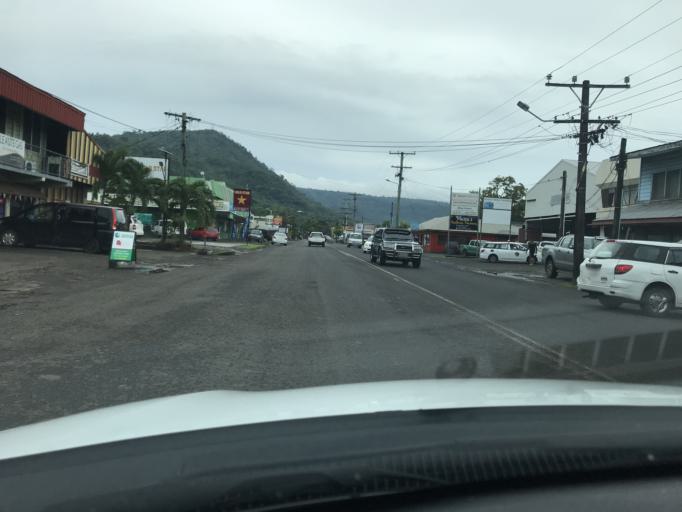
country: WS
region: Tuamasaga
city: Apia
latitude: -13.8352
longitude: -171.7702
